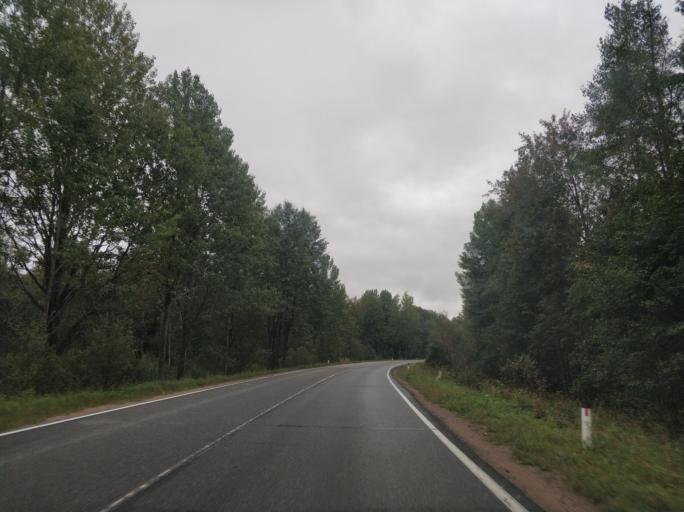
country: RU
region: Leningrad
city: Borisova Griva
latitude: 60.1336
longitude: 30.9616
